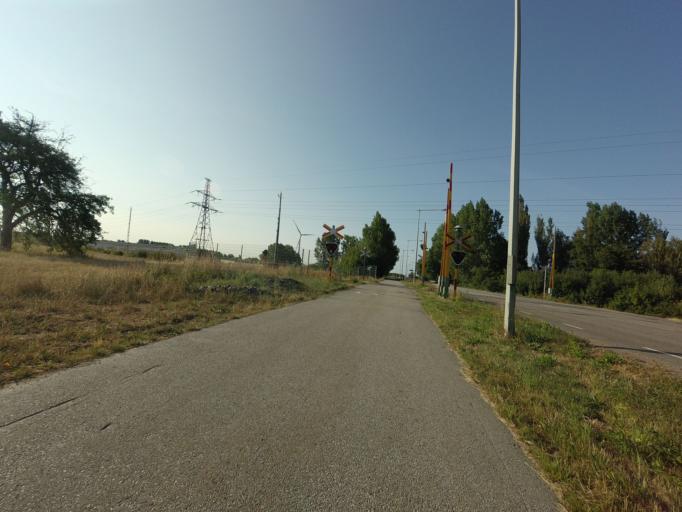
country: SE
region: Skane
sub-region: Landskrona
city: Landskrona
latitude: 55.8673
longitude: 12.8699
